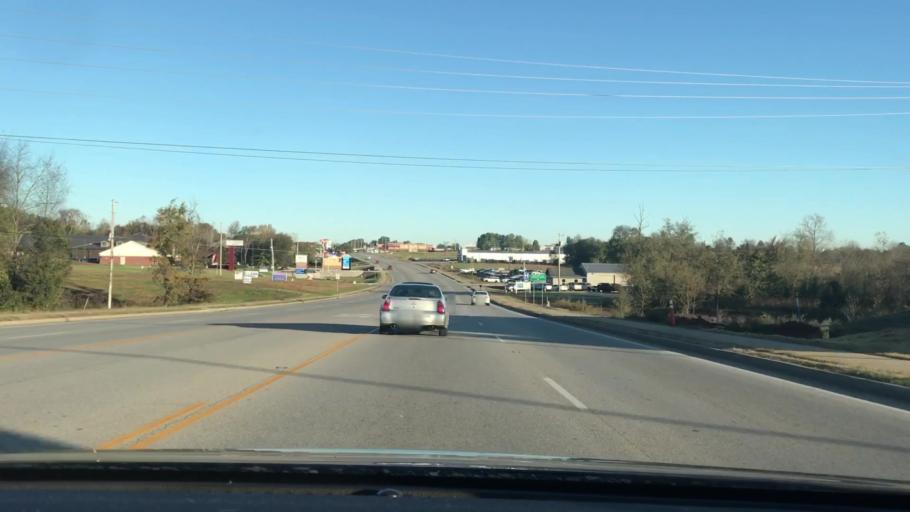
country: US
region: Kentucky
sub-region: Simpson County
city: Franklin
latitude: 36.6983
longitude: -86.5718
